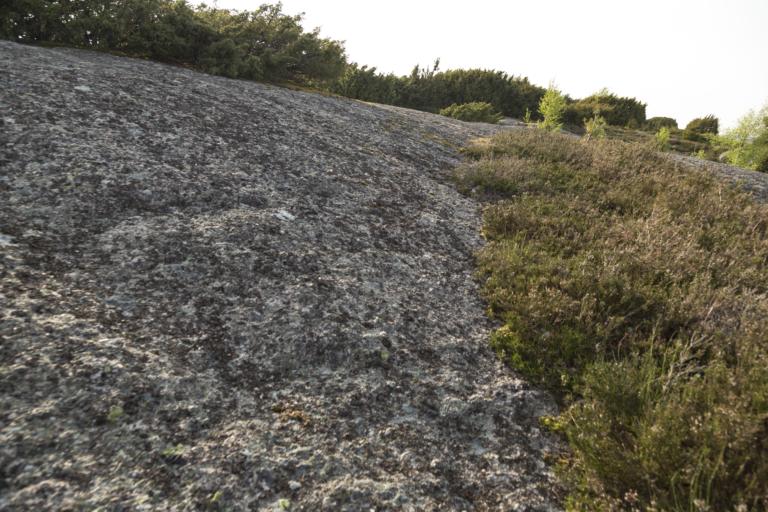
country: SE
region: Halland
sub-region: Varbergs Kommun
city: Varberg
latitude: 57.1598
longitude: 12.2392
